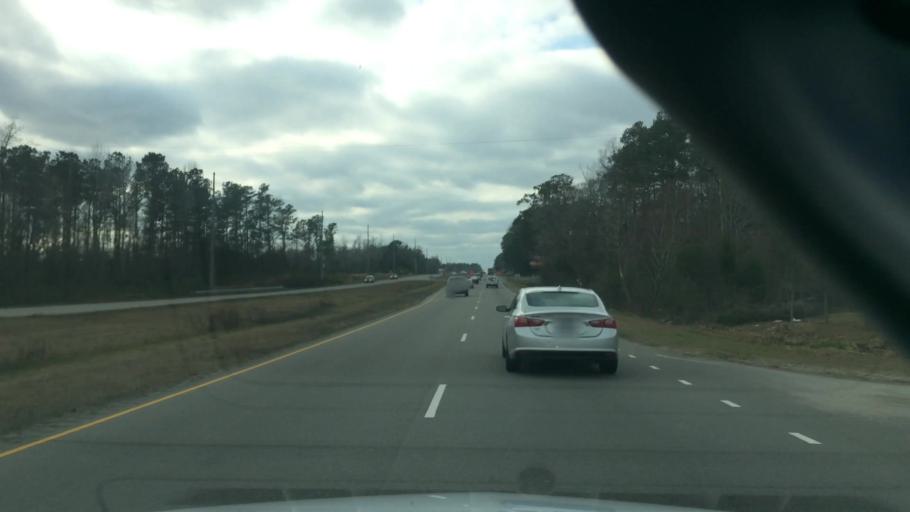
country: US
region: North Carolina
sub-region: Brunswick County
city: Shallotte
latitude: 33.9913
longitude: -78.3481
